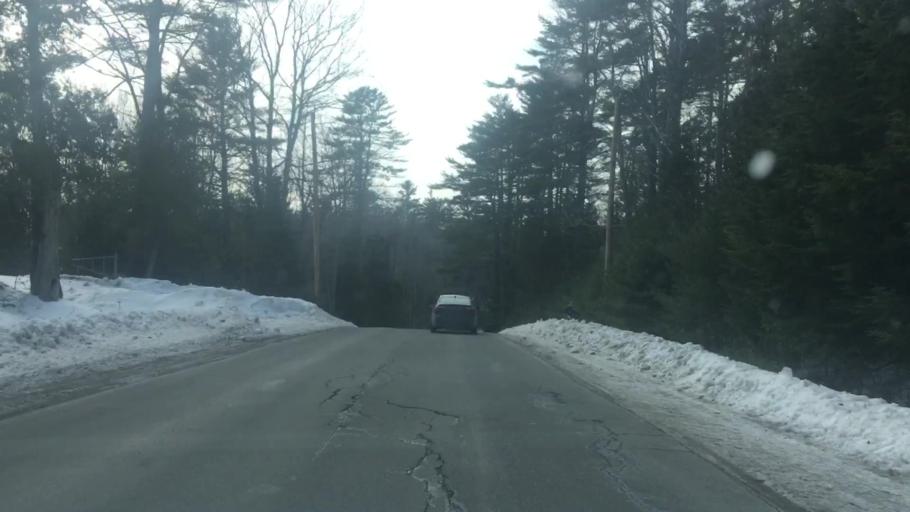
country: US
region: Maine
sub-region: Hancock County
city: Orland
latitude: 44.6207
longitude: -68.7032
